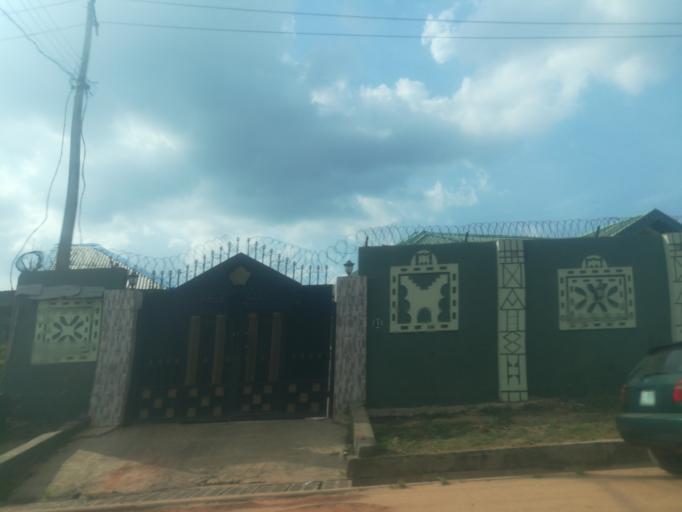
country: NG
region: Ogun
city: Abeokuta
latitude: 7.1121
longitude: 3.3127
